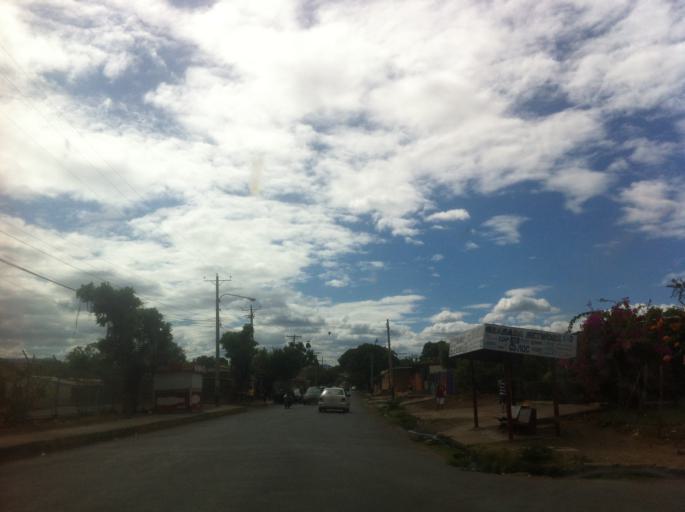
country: NI
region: Granada
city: Granada
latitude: 11.9407
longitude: -85.9483
